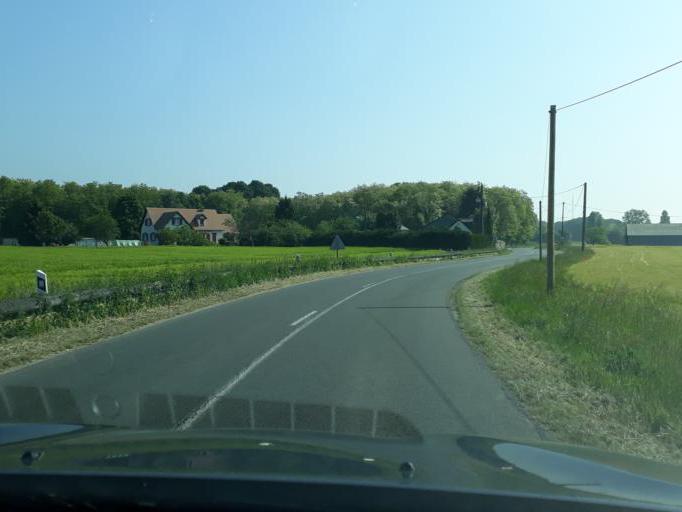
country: FR
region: Centre
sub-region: Departement du Loiret
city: Vennecy
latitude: 47.9518
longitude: 2.0732
